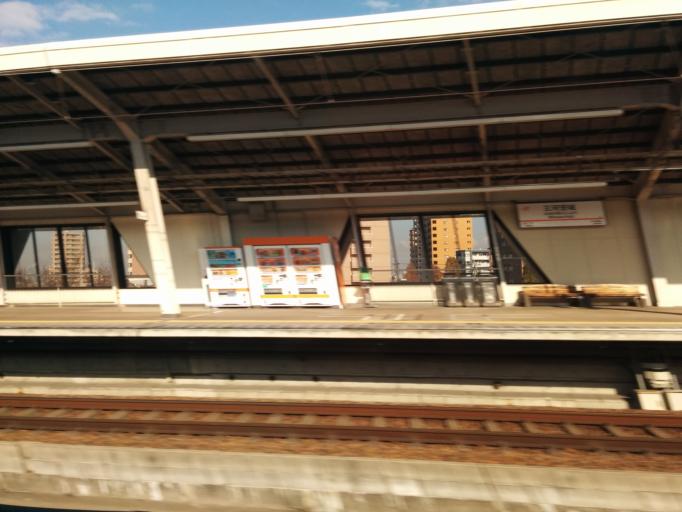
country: JP
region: Aichi
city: Anjo
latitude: 34.9688
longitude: 137.0608
